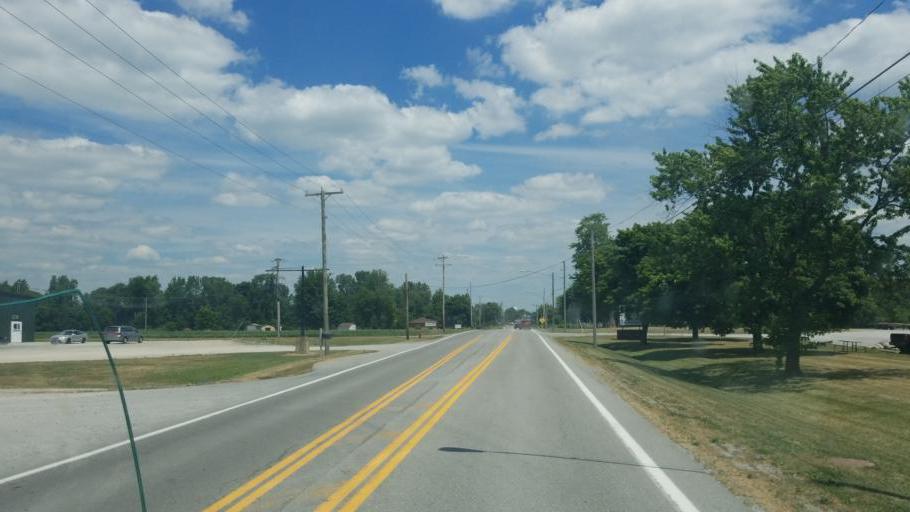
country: US
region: Ohio
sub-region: Defiance County
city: Hicksville
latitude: 41.2835
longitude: -84.7809
